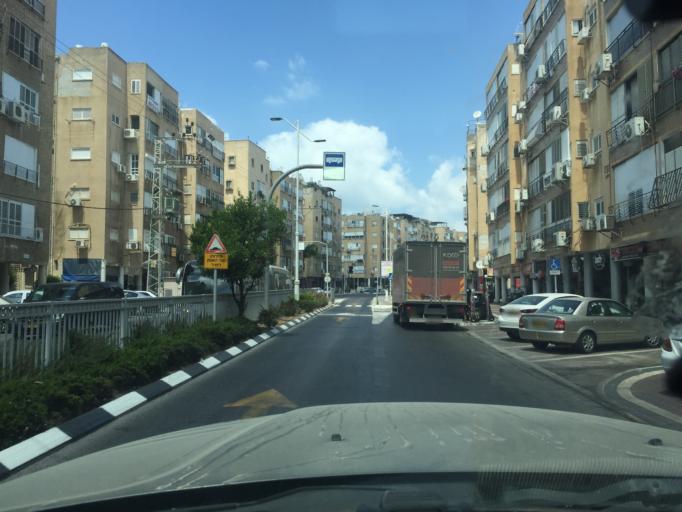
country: IL
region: Tel Aviv
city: Bat Yam
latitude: 32.0132
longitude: 34.7423
